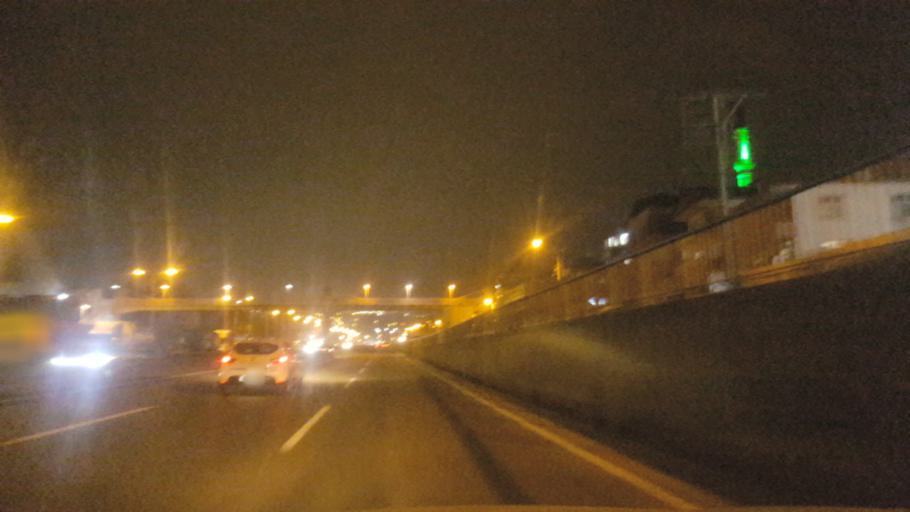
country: TR
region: Kocaeli
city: Tavsancil
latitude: 40.7825
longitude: 29.5384
